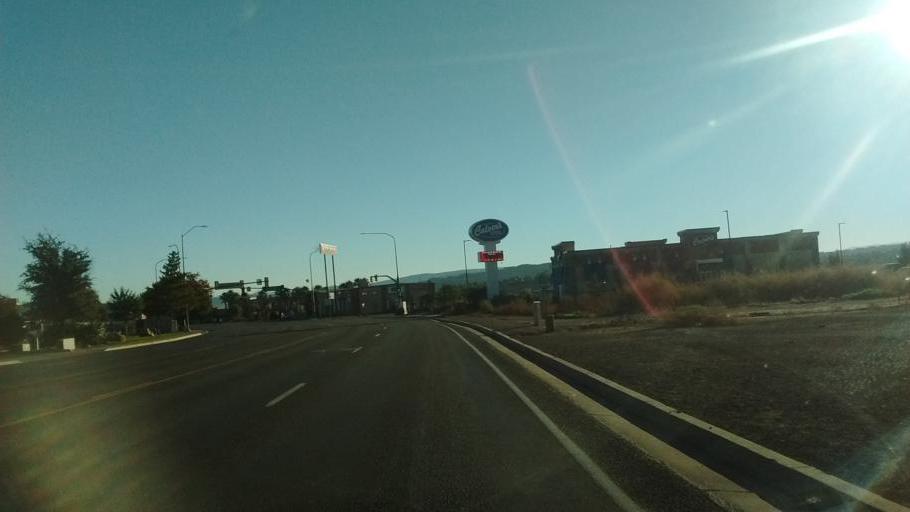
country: US
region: Utah
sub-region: Washington County
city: Saint George
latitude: 37.0814
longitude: -113.5795
